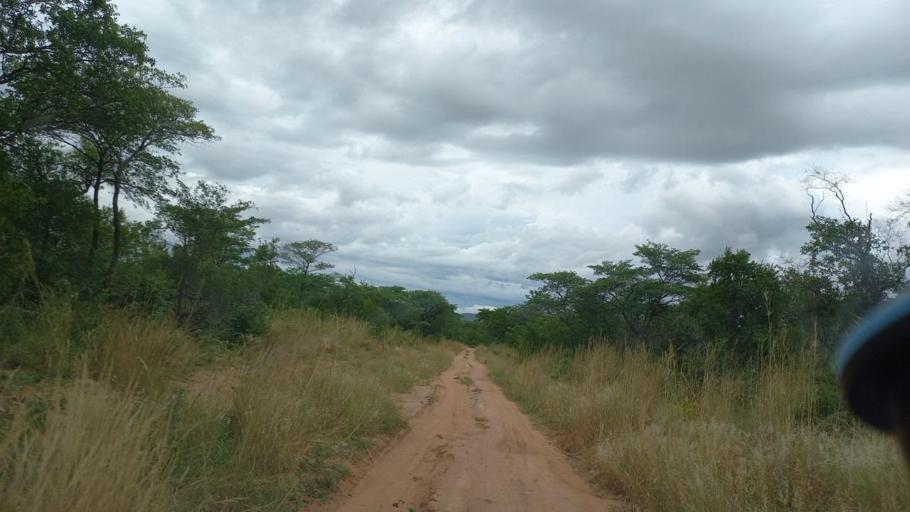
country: ZM
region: Lusaka
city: Luangwa
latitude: -15.5652
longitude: 30.3241
